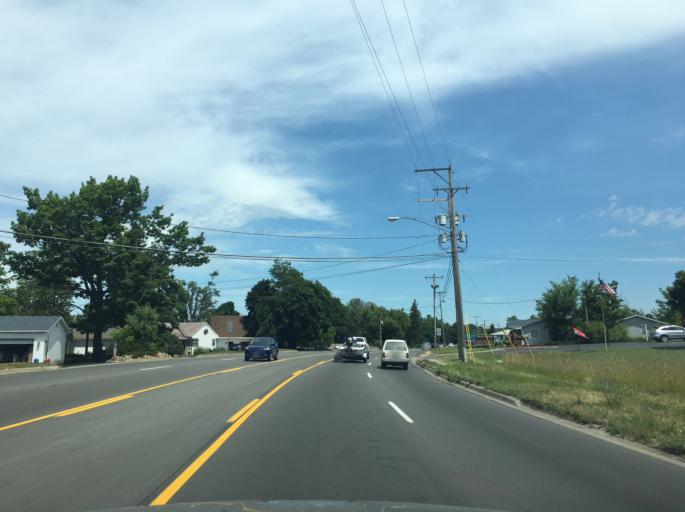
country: US
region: Michigan
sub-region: Grand Traverse County
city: Traverse City
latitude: 44.7691
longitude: -85.5036
